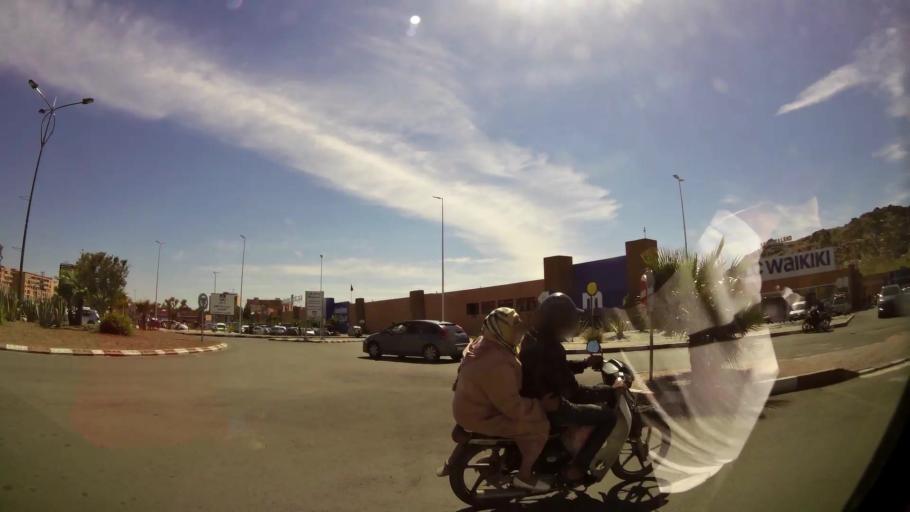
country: MA
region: Marrakech-Tensift-Al Haouz
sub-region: Marrakech
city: Marrakesh
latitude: 31.6690
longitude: -8.0121
